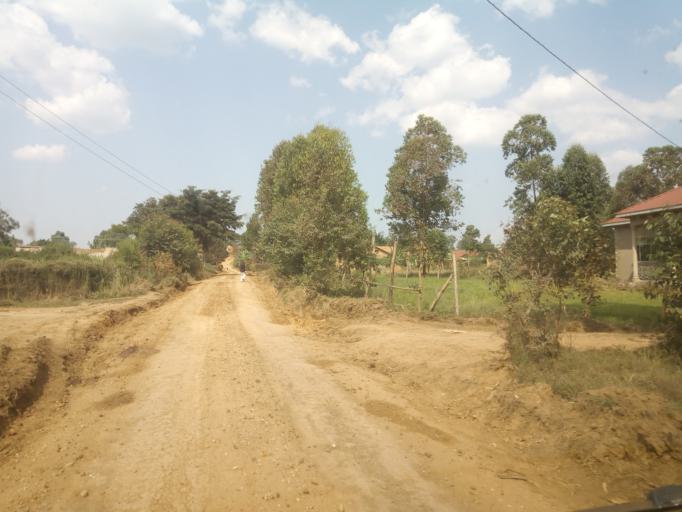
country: UG
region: Western Region
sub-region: Kanungu District
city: Ntungamo
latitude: -0.7838
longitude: 29.6980
